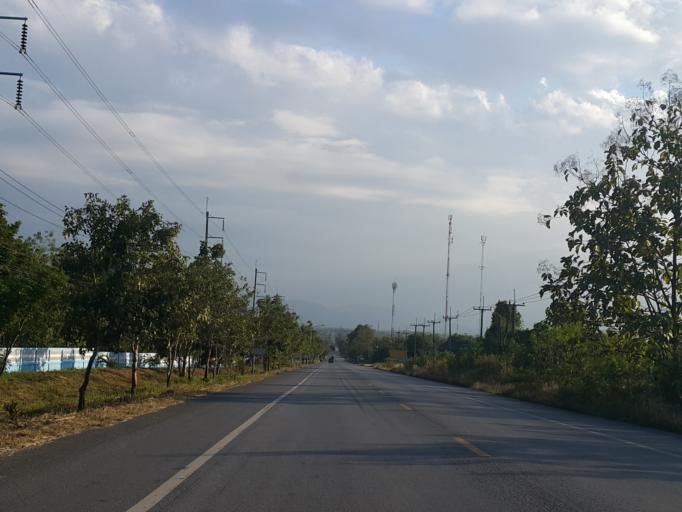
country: TH
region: Lampang
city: Lampang
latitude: 18.4251
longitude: 99.5419
